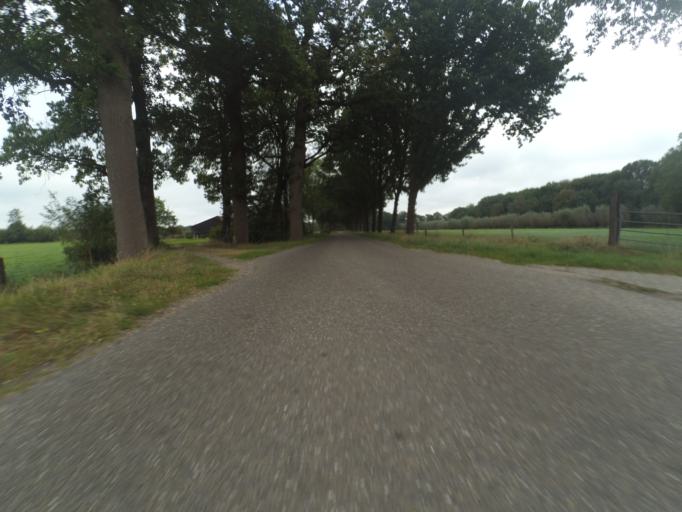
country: NL
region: Utrecht
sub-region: Gemeente Utrechtse Heuvelrug
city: Overberg
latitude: 52.0707
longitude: 5.4850
